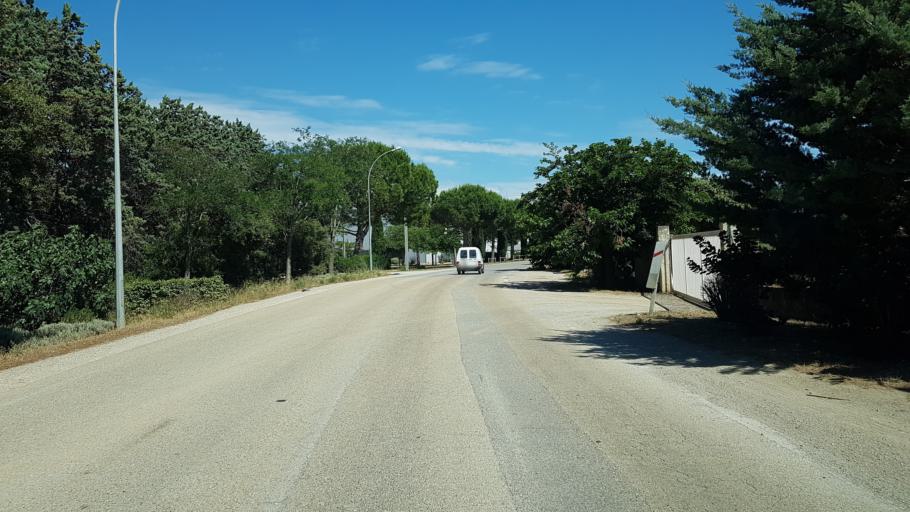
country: FR
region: Provence-Alpes-Cote d'Azur
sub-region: Departement des Bouches-du-Rhone
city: Saint-Martin-de-Crau
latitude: 43.6216
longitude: 4.7908
